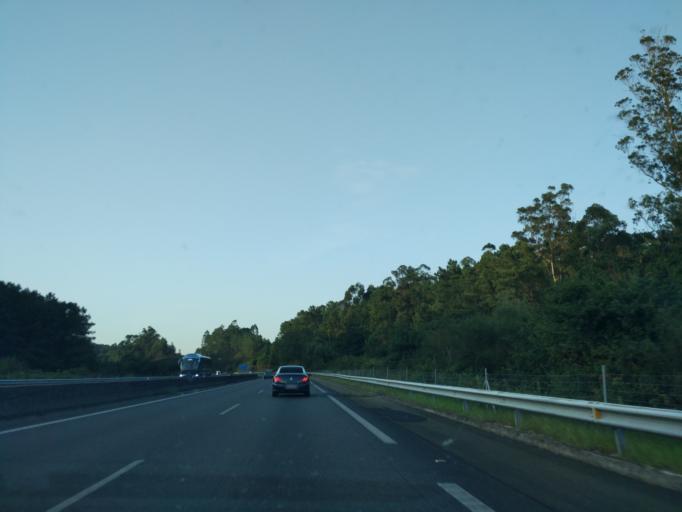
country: ES
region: Galicia
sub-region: Provincia de Pontevedra
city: Caldas de Reis
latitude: 42.6311
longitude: -8.6595
